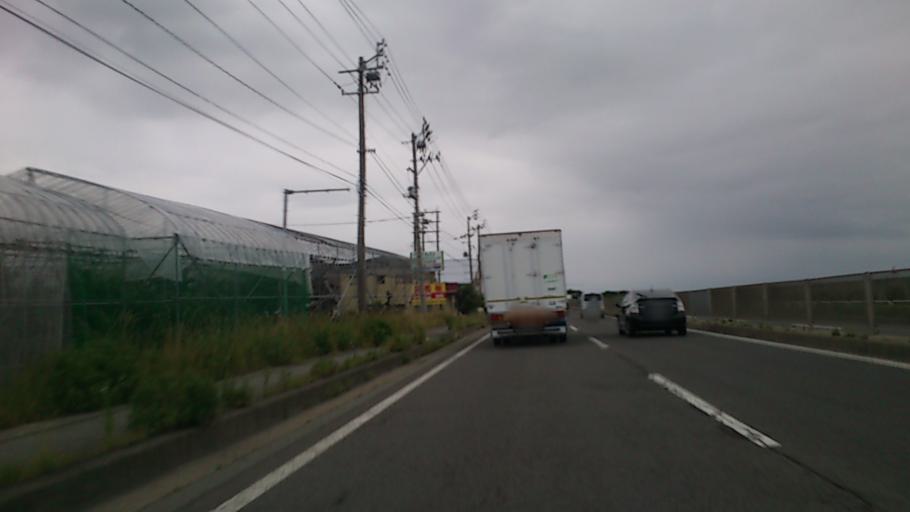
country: JP
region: Yamagata
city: Higashine
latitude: 38.4092
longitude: 140.3740
